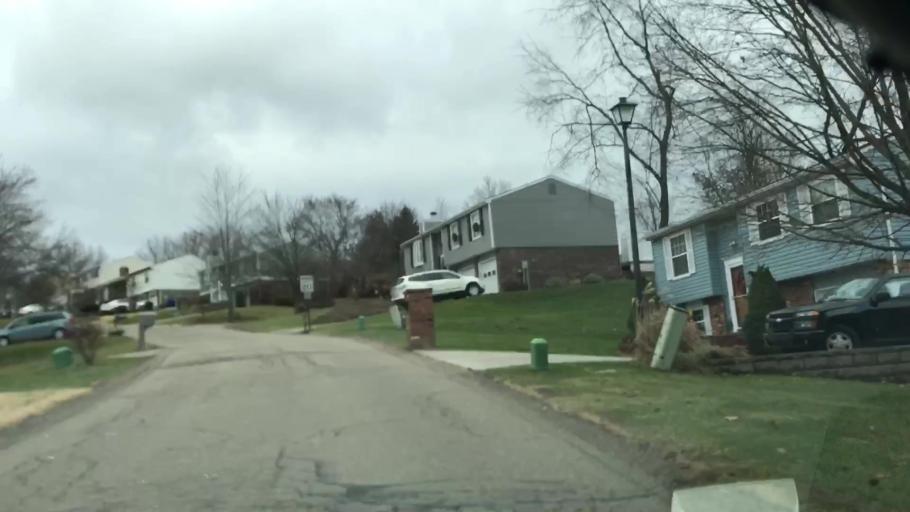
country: US
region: Pennsylvania
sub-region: Allegheny County
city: Enlow
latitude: 40.4462
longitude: -80.2210
